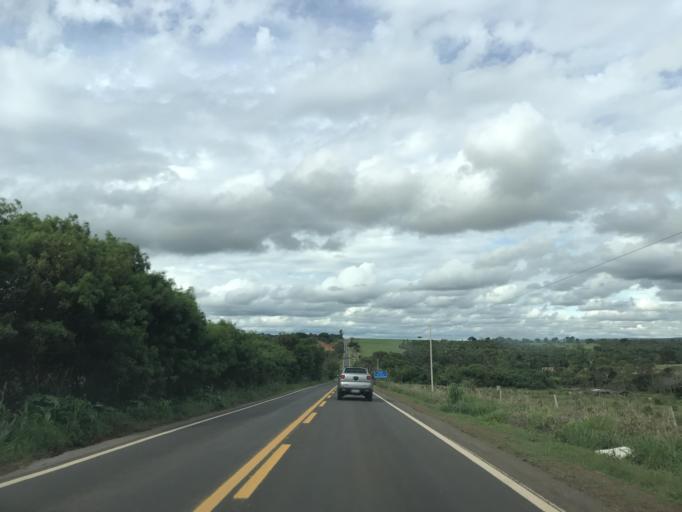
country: BR
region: Goias
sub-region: Piracanjuba
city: Piracanjuba
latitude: -17.1984
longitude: -48.7005
